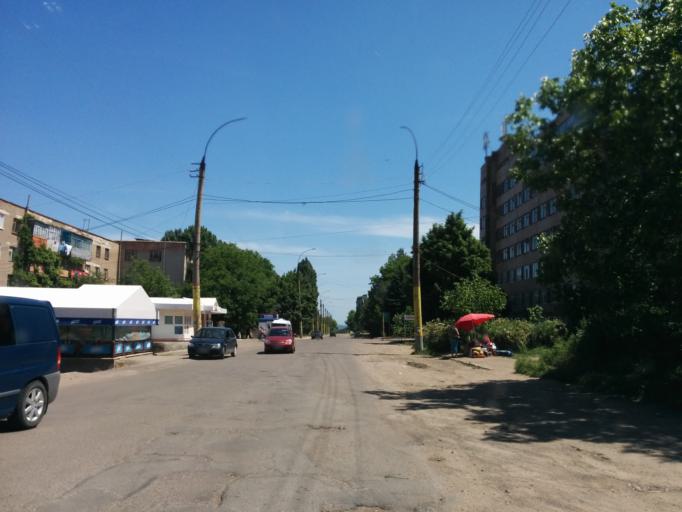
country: MD
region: Raionul Soroca
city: Soroca
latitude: 48.1627
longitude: 28.2684
